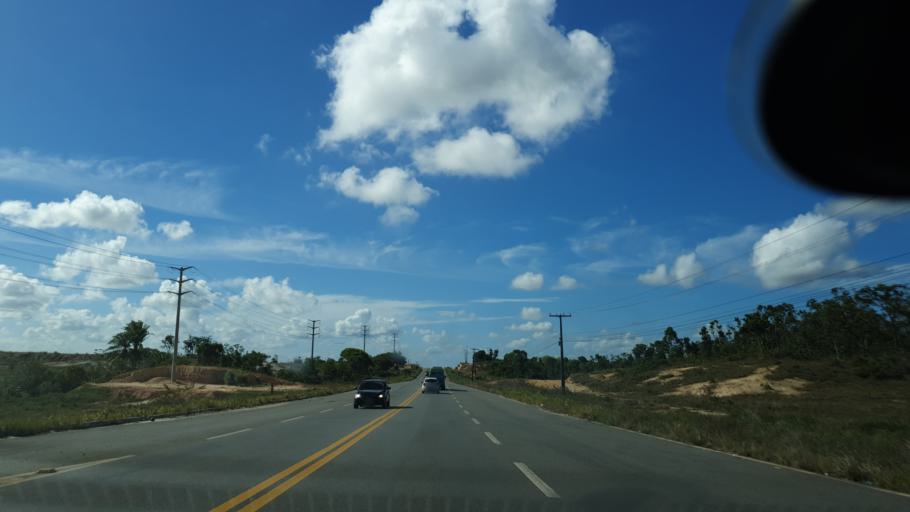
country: BR
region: Bahia
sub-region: Camacari
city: Camacari
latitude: -12.6971
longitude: -38.2201
